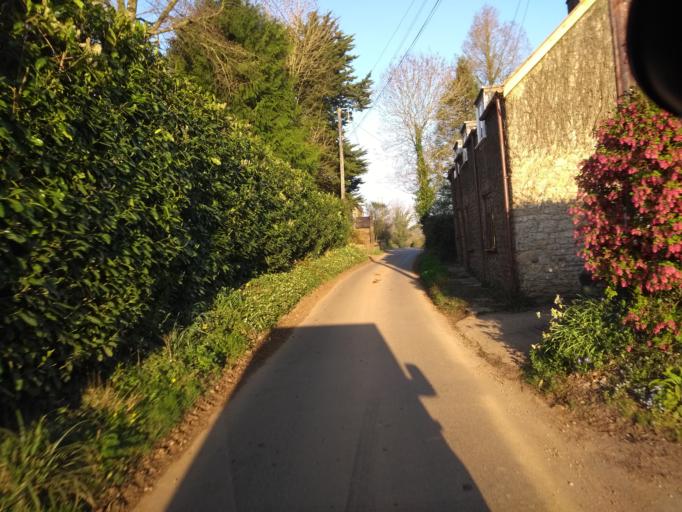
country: GB
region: England
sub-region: Somerset
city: Crewkerne
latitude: 50.8359
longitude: -2.7959
